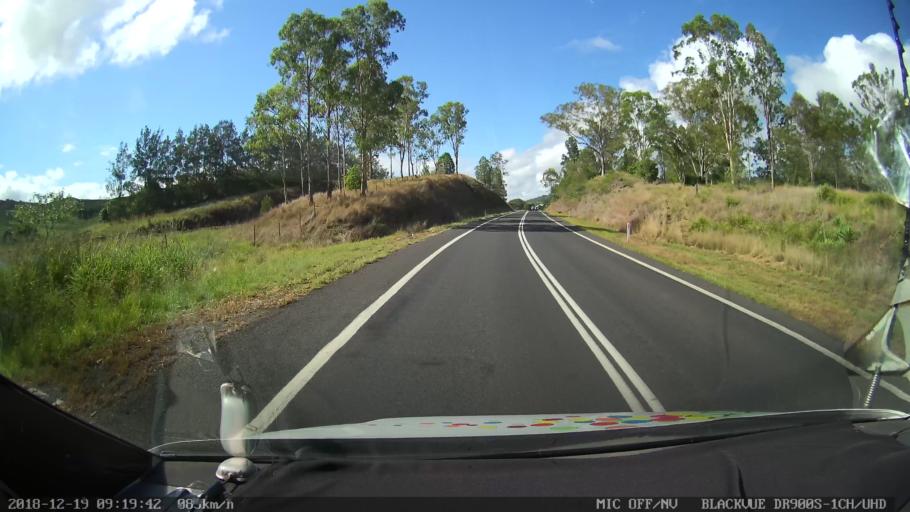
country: AU
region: New South Wales
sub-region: Kyogle
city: Kyogle
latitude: -28.5634
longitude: 152.9783
